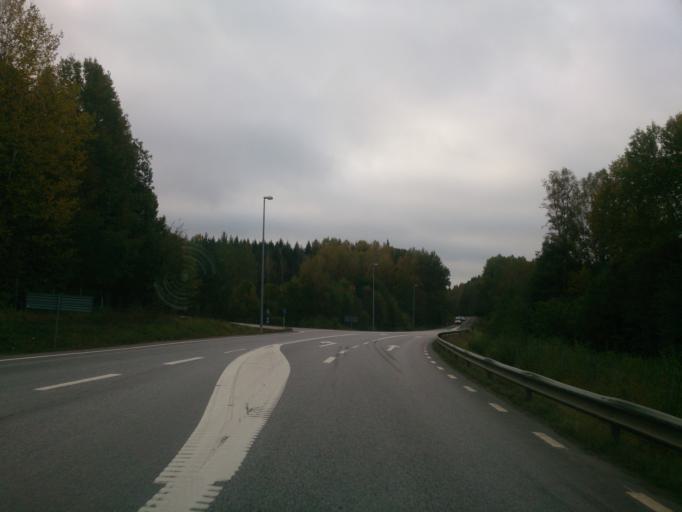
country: SE
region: OEstergoetland
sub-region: Atvidabergs Kommun
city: Atvidaberg
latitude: 58.1840
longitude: 16.0238
